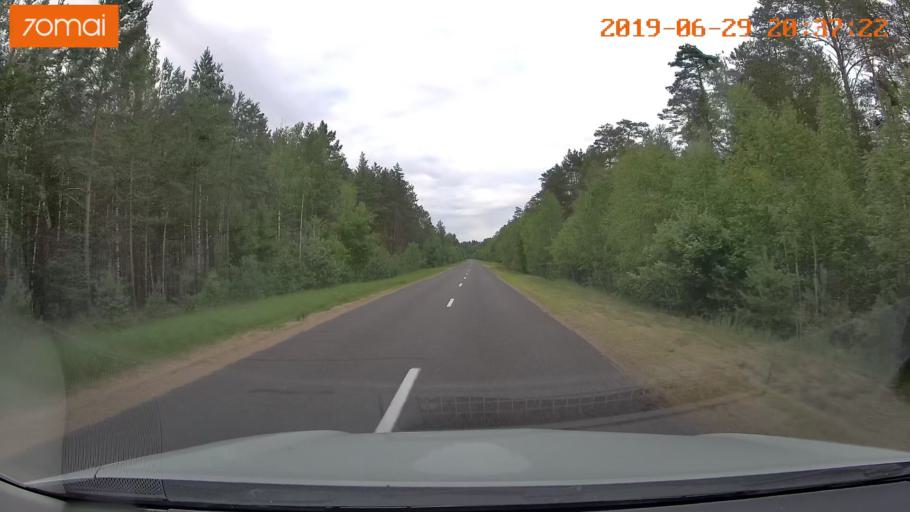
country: BY
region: Brest
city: Hantsavichy
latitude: 52.5370
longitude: 26.3641
